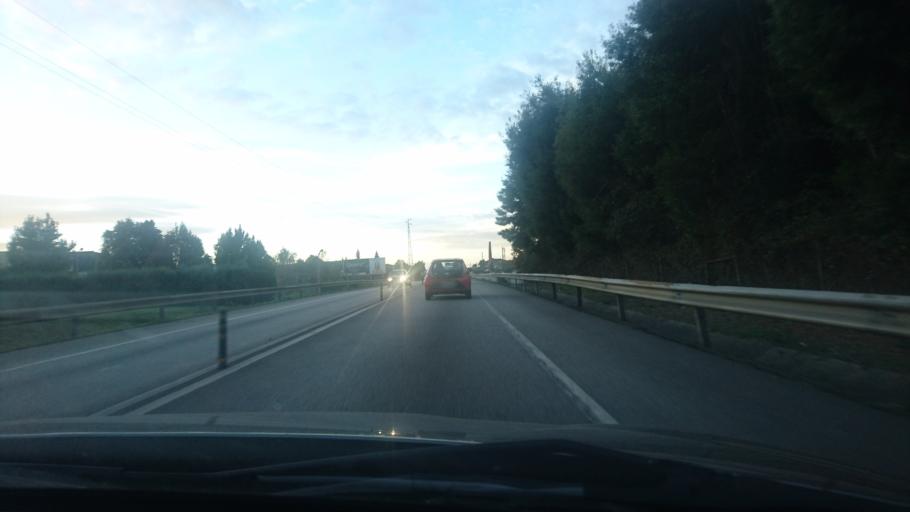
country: PT
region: Aveiro
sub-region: Sao Joao da Madeira
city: Sao Joao da Madeira
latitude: 40.8987
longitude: -8.4819
